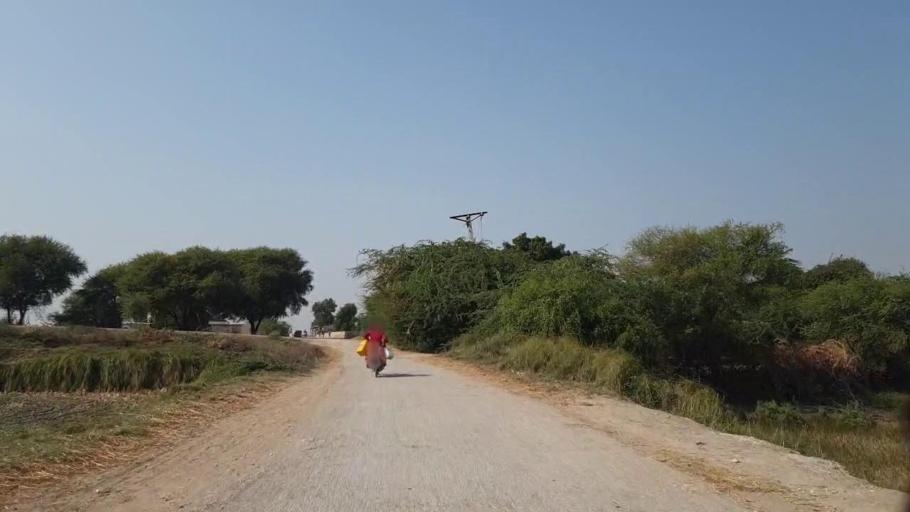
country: PK
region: Sindh
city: Bulri
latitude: 24.9602
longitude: 68.3293
